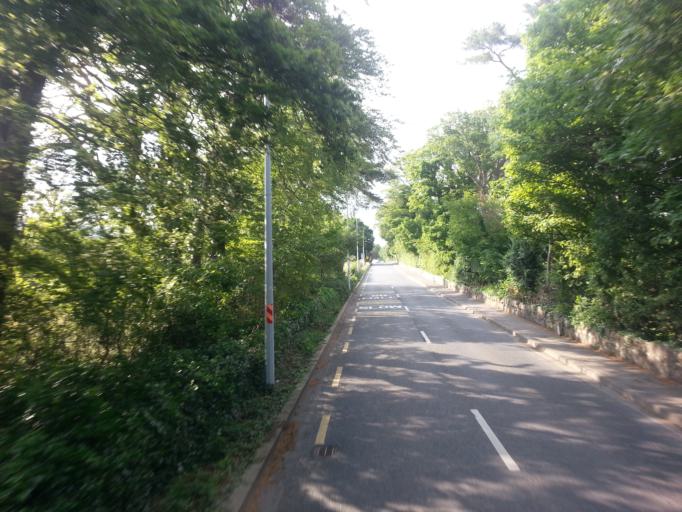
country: IE
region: Leinster
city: Foxrock
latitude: 53.2304
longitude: -6.1872
